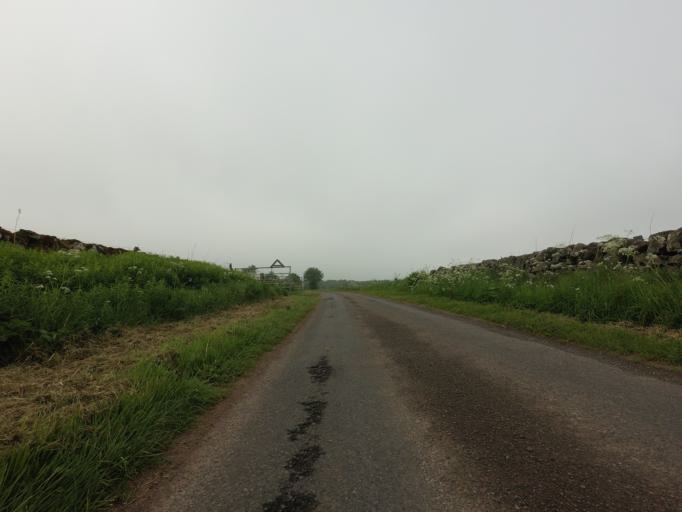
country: GB
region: Scotland
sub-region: Fife
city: Ballingry
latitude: 56.2492
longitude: -3.3352
